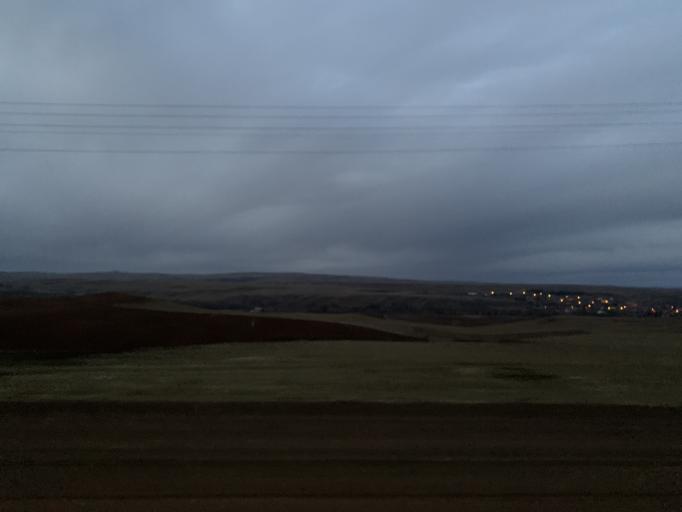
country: TR
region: Yozgat
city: Yenipazar
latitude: 39.4716
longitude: 35.0994
